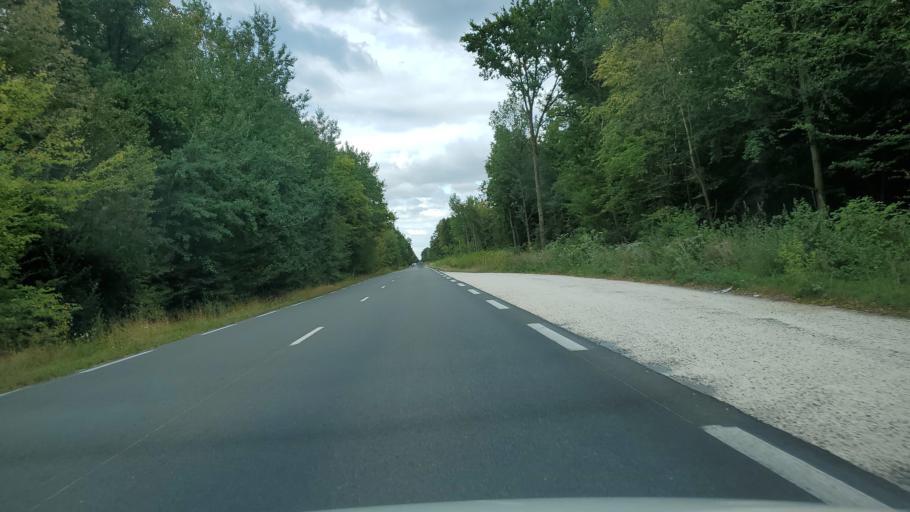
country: FR
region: Ile-de-France
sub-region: Departement de Seine-et-Marne
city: Mortcerf
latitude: 48.7633
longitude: 2.9234
